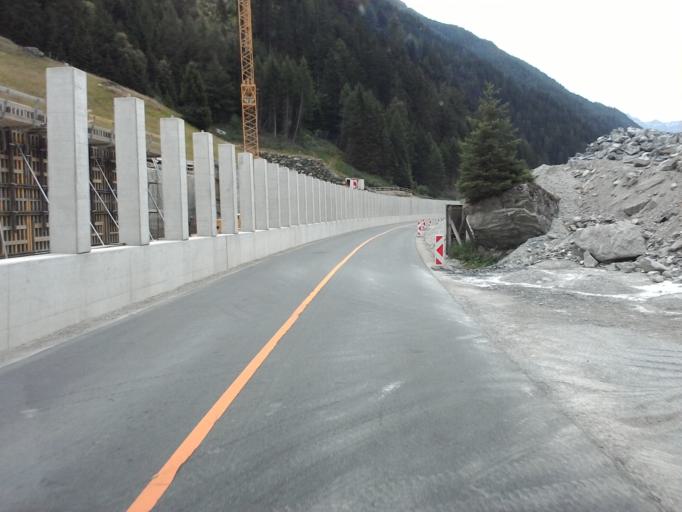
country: AT
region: Tyrol
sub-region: Politischer Bezirk Lienz
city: Matrei in Osttirol
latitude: 47.0732
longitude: 12.5321
